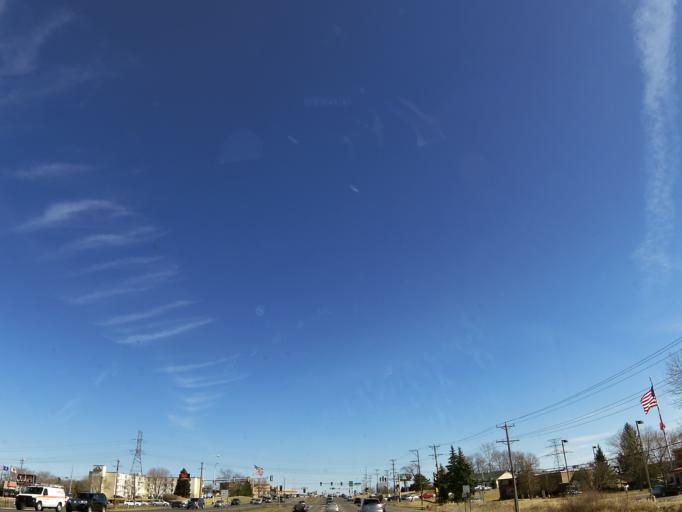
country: US
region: Minnesota
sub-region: Hennepin County
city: Plymouth
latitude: 45.0126
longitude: -93.4634
